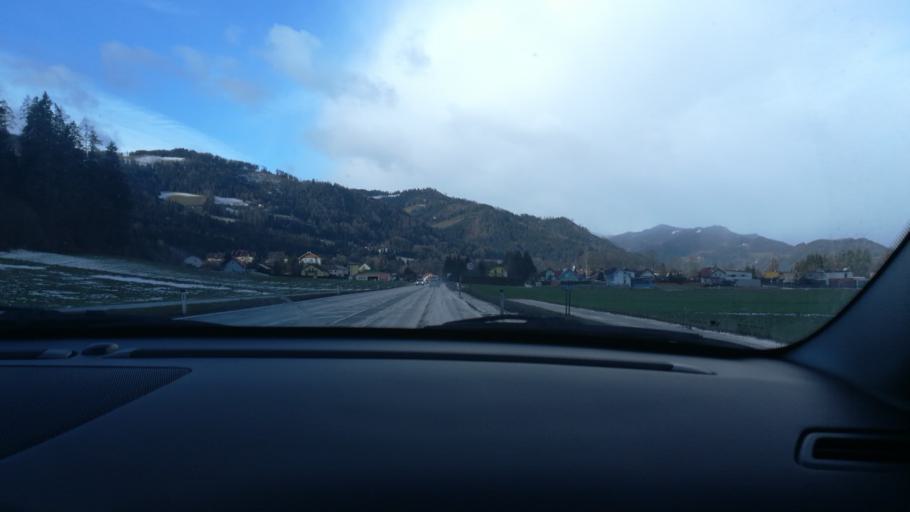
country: AT
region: Styria
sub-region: Politischer Bezirk Murtal
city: Oberweg
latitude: 47.1741
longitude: 14.6175
